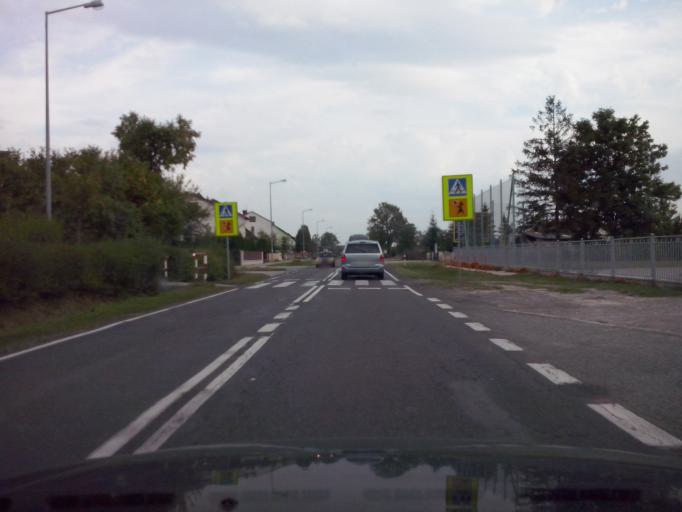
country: PL
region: Lublin Voivodeship
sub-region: Powiat bilgorajski
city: Bilgoraj
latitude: 50.5066
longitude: 22.7205
